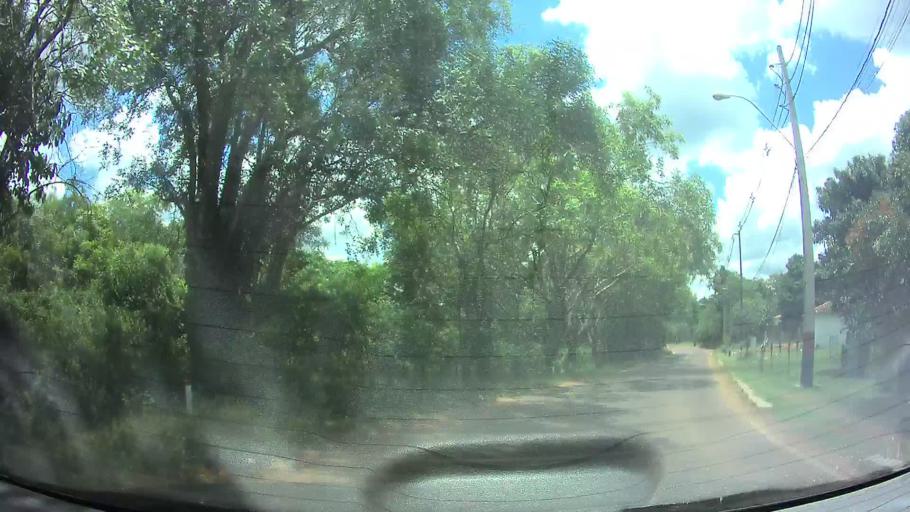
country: PY
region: Central
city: Capiata
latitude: -25.3082
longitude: -57.4368
